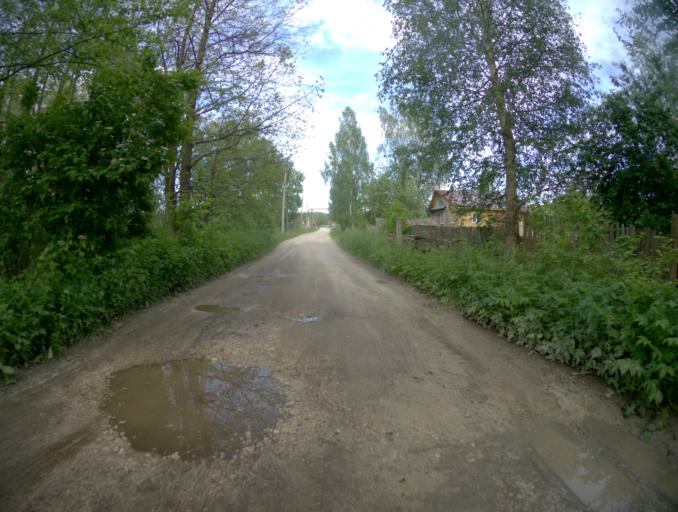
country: RU
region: Vladimir
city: Zolotkovo
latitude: 55.3984
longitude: 40.9102
